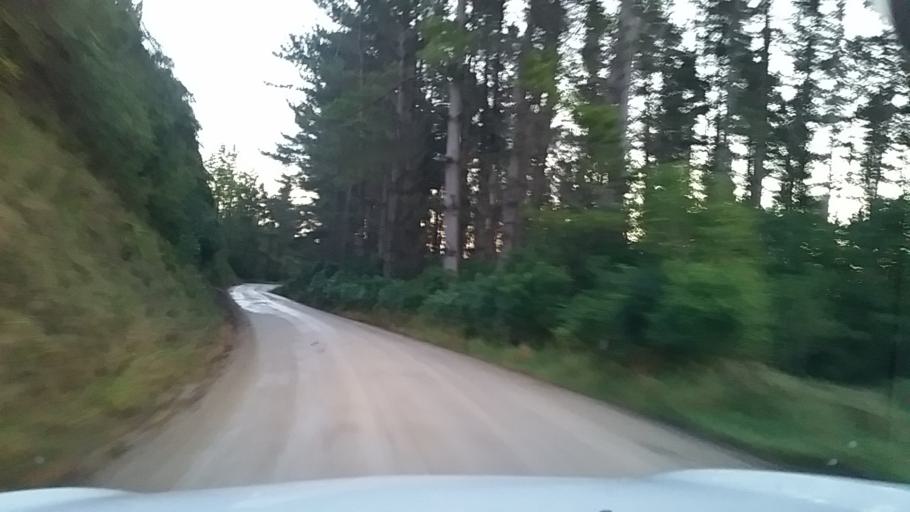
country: NZ
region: Manawatu-Wanganui
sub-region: Wanganui District
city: Wanganui
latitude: -39.7743
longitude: 174.8607
